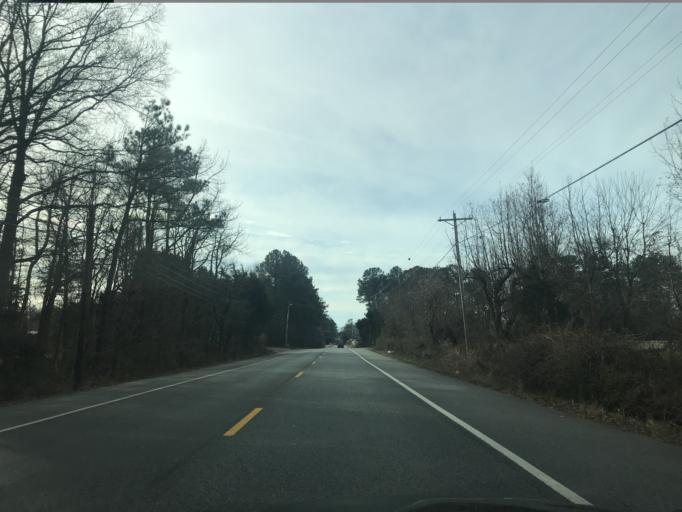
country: US
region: Maryland
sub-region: Charles County
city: Cobb Island
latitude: 38.2752
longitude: -76.8566
